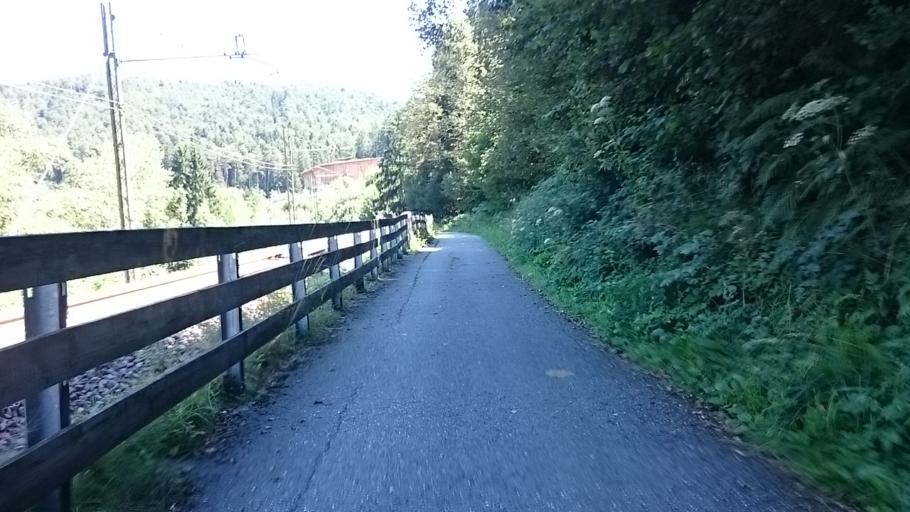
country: IT
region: Trentino-Alto Adige
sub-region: Bolzano
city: Falzes
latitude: 46.7854
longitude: 11.8686
